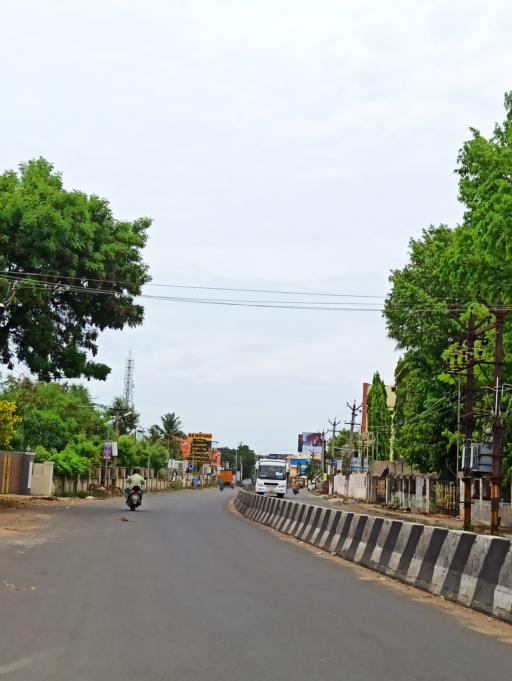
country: IN
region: Tamil Nadu
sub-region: Kancheepuram
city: Vandalur
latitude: 12.9195
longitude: 80.0848
